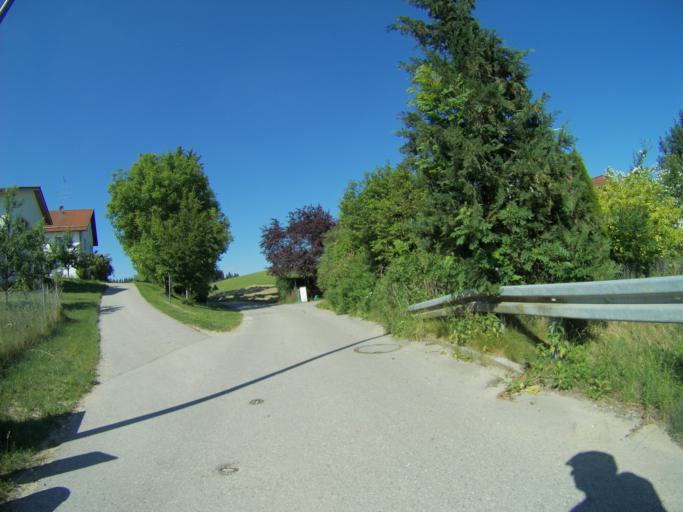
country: DE
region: Bavaria
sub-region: Upper Bavaria
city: Kranzberg
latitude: 48.3992
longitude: 11.6741
